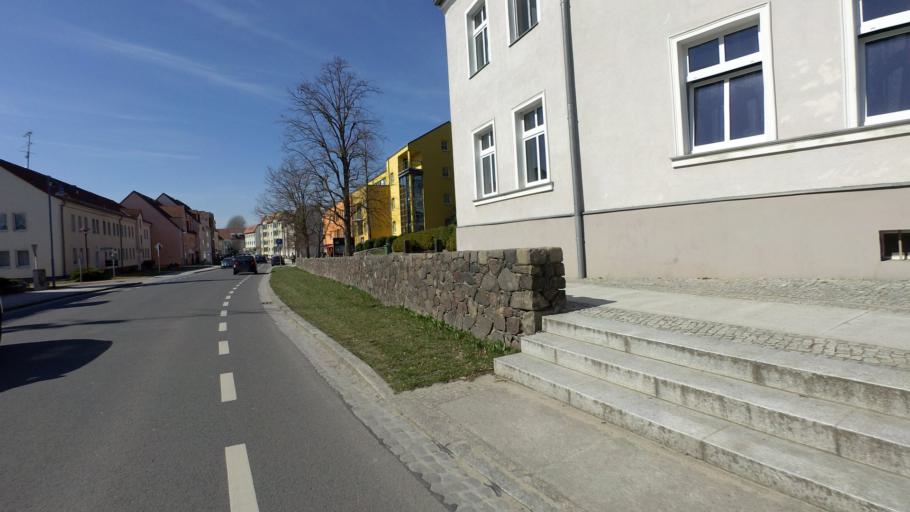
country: DE
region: Brandenburg
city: Muncheberg
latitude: 52.5019
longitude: 14.1431
